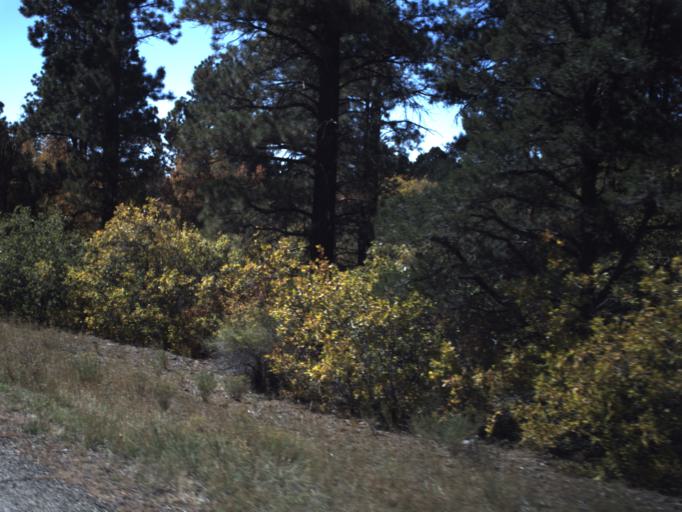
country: US
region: Utah
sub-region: Wayne County
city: Loa
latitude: 37.9852
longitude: -111.4305
